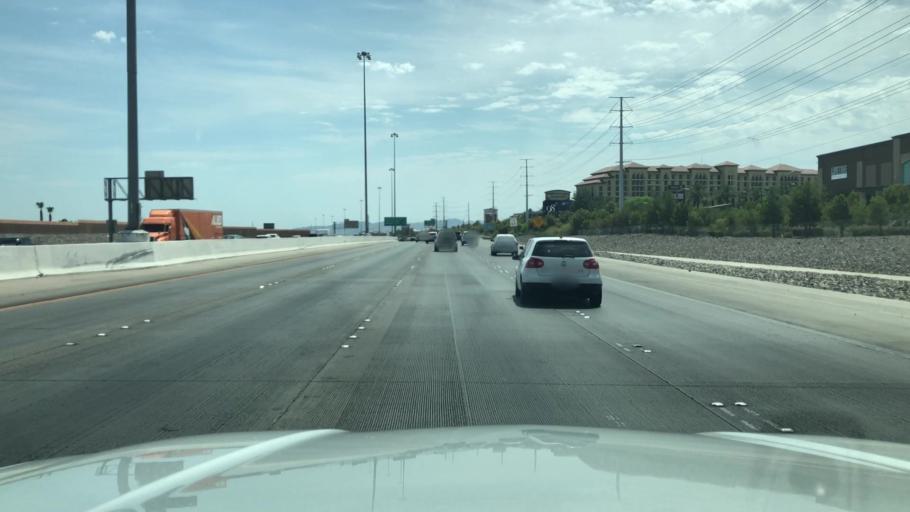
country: US
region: Nevada
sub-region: Clark County
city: Whitney
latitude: 36.0234
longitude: -115.0954
